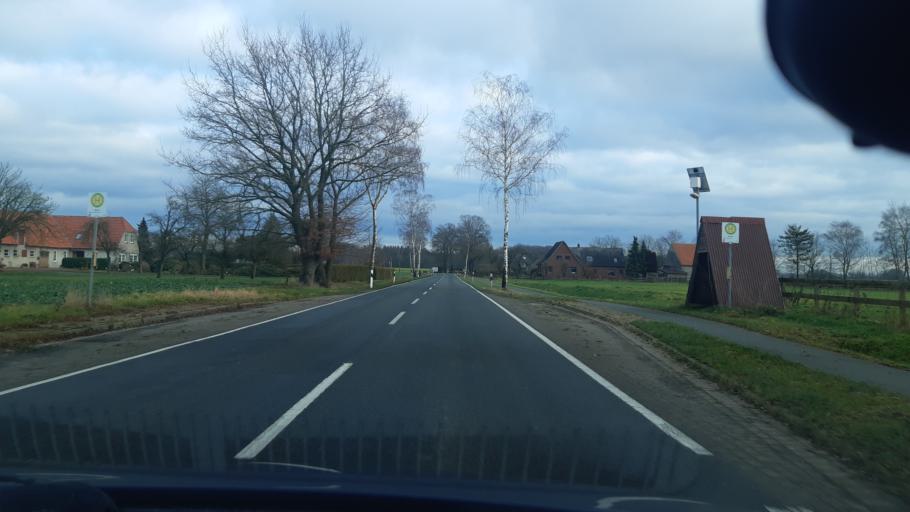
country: DE
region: Lower Saxony
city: Harpstedt
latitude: 52.8986
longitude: 8.5567
